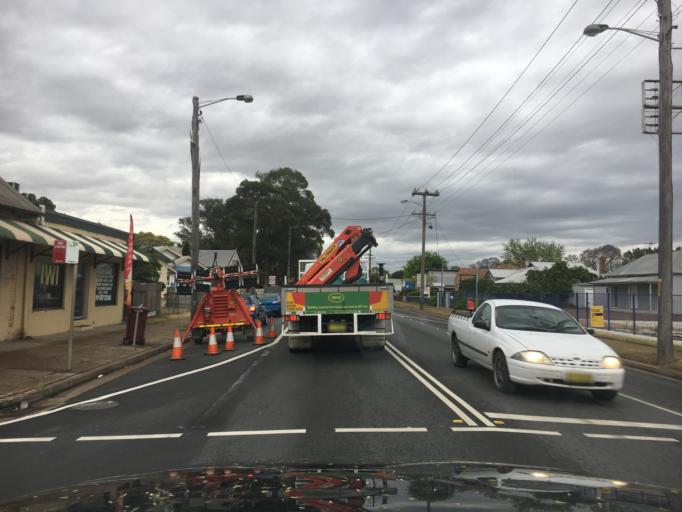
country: AU
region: New South Wales
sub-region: Singleton
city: Singleton
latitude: -32.5682
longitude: 151.1795
